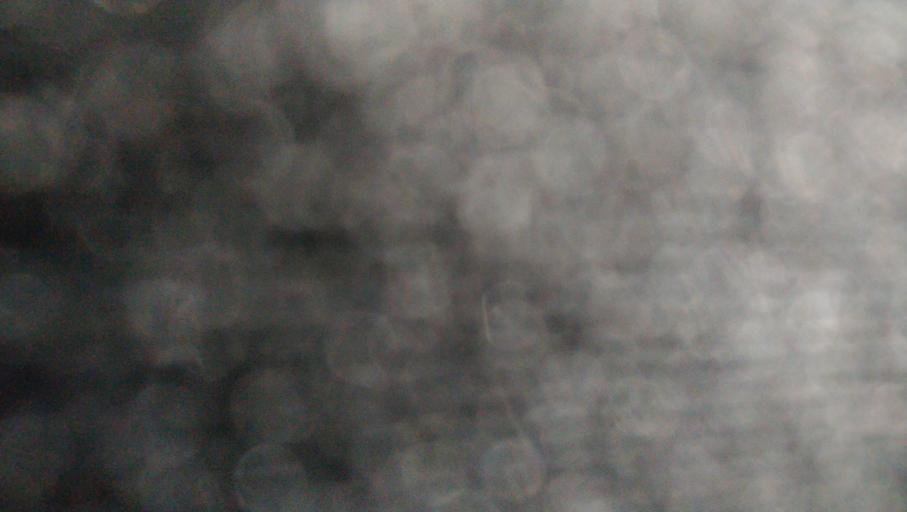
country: MX
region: Oaxaca
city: Juchitan de Zaragoza
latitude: 16.4475
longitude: -95.0239
